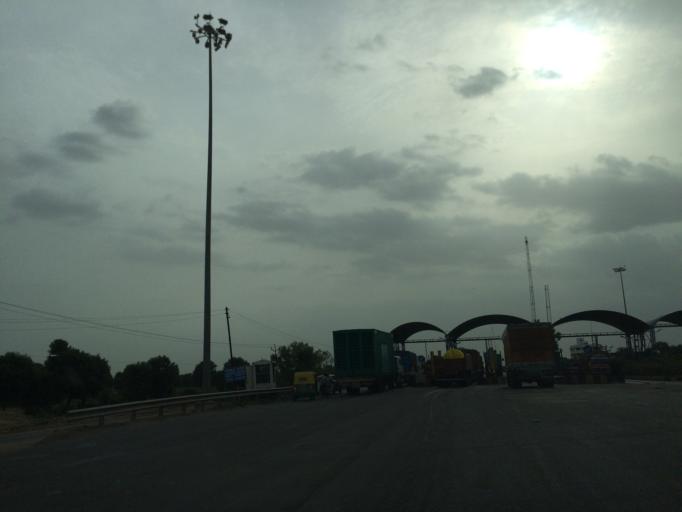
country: IN
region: Gujarat
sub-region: Ahmadabad
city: Sarkhej
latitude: 22.9347
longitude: 72.5207
